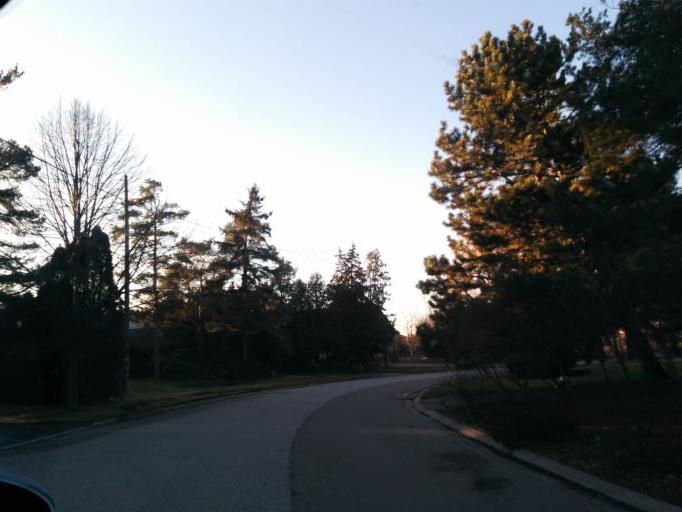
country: CA
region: Ontario
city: Mississauga
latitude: 43.5593
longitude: -79.6218
